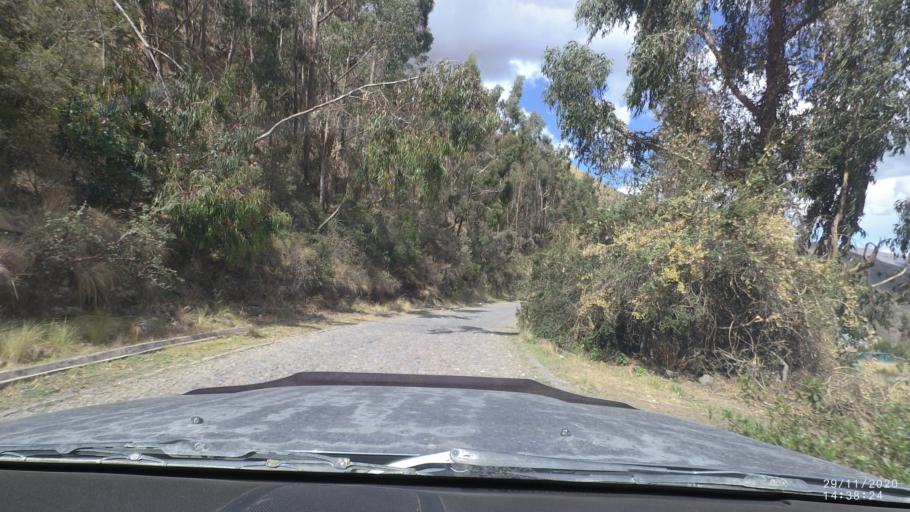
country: BO
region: Cochabamba
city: Sipe Sipe
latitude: -17.2726
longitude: -66.3304
